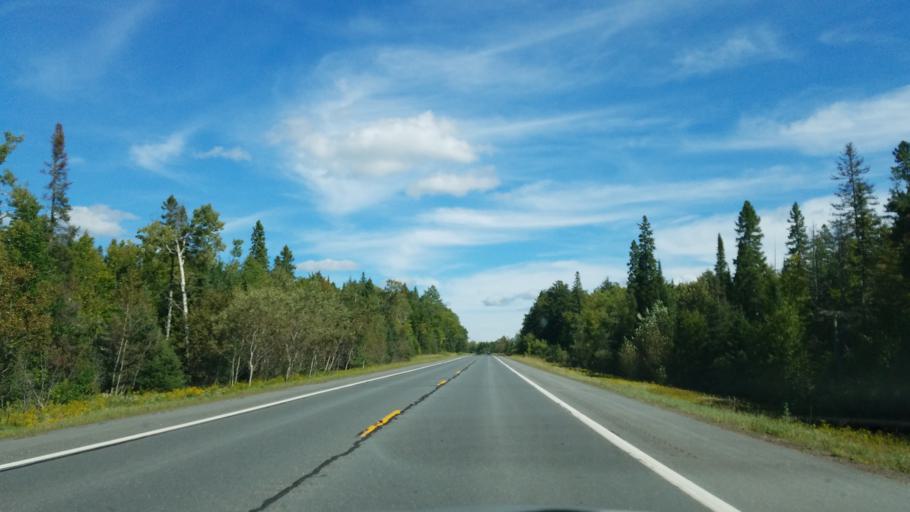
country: US
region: Michigan
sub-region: Baraga County
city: L'Anse
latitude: 46.5806
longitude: -88.4602
